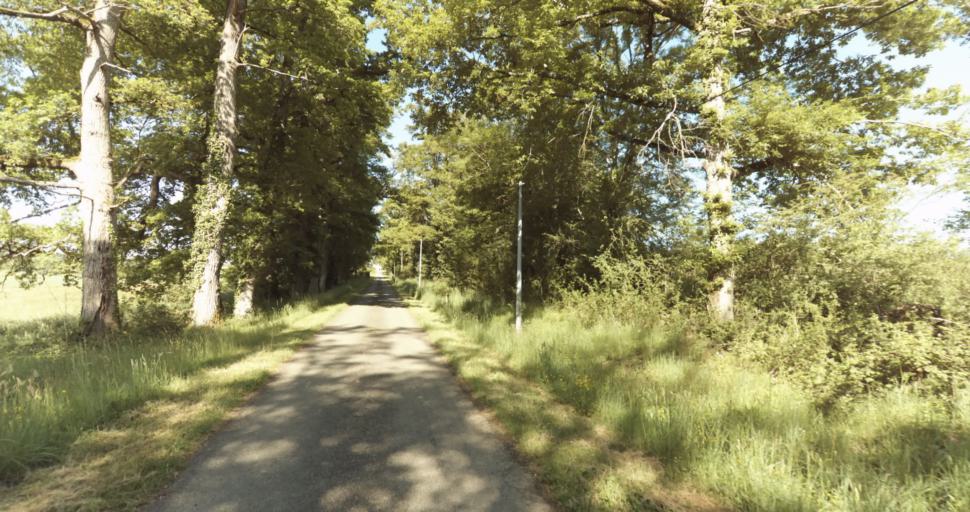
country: FR
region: Limousin
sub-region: Departement de la Haute-Vienne
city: Le Vigen
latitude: 45.7110
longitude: 1.2720
